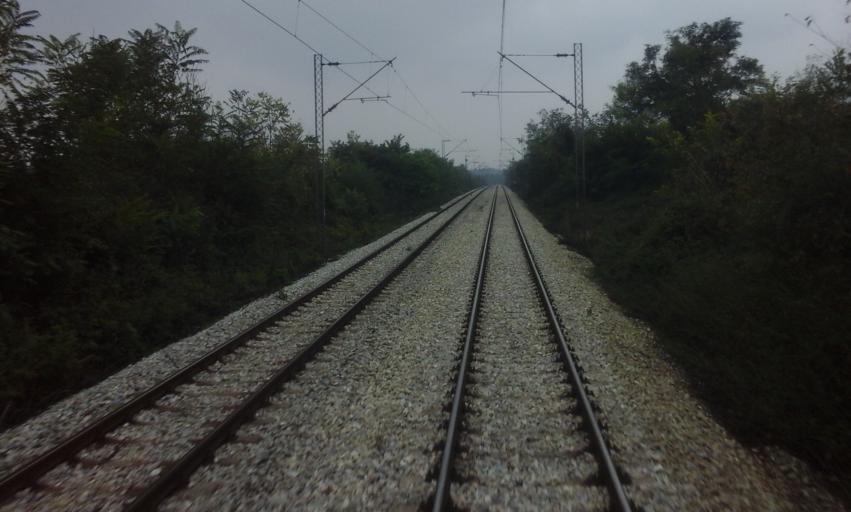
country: RS
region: Central Serbia
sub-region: Sumadijski Okrug
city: Lapovo
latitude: 44.2151
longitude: 21.0942
